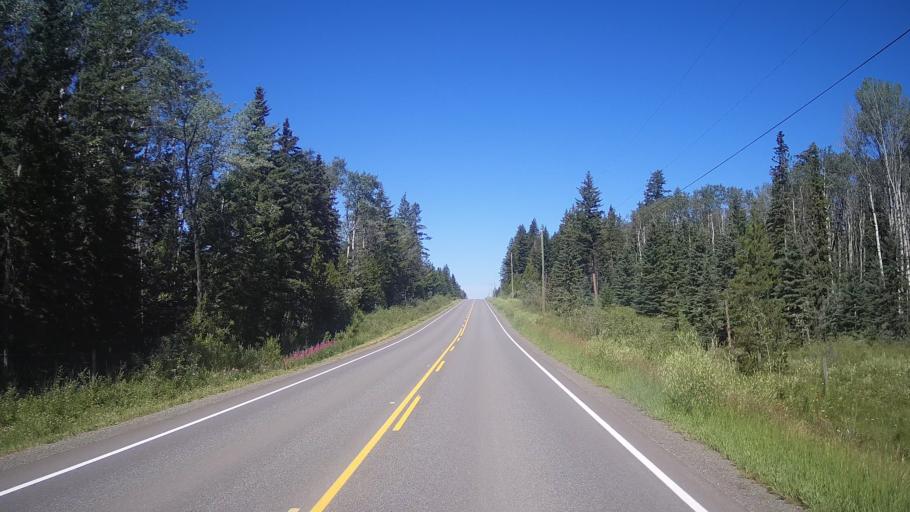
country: CA
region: British Columbia
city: Cache Creek
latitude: 51.5410
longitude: -121.0526
